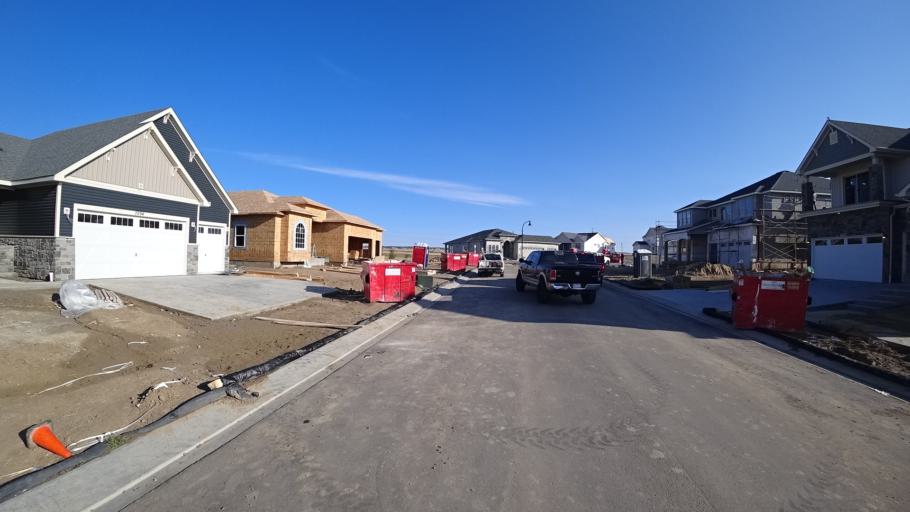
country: US
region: Colorado
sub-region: El Paso County
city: Cimarron Hills
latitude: 38.9343
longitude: -104.6538
